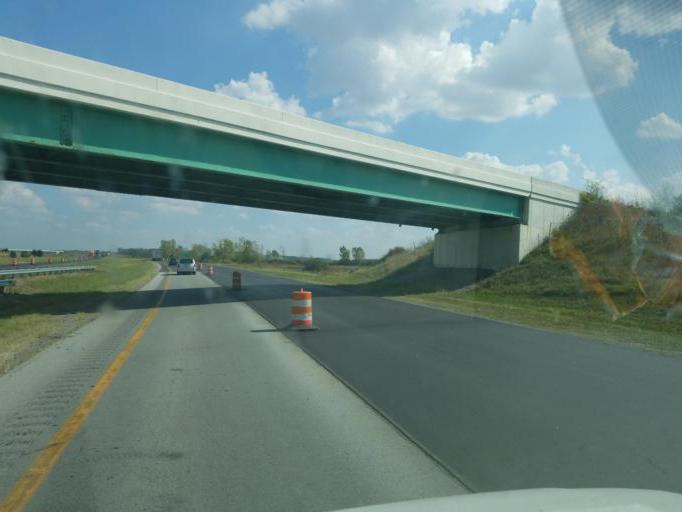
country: US
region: Ohio
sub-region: Van Wert County
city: Van Wert
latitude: 40.8713
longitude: -84.5144
